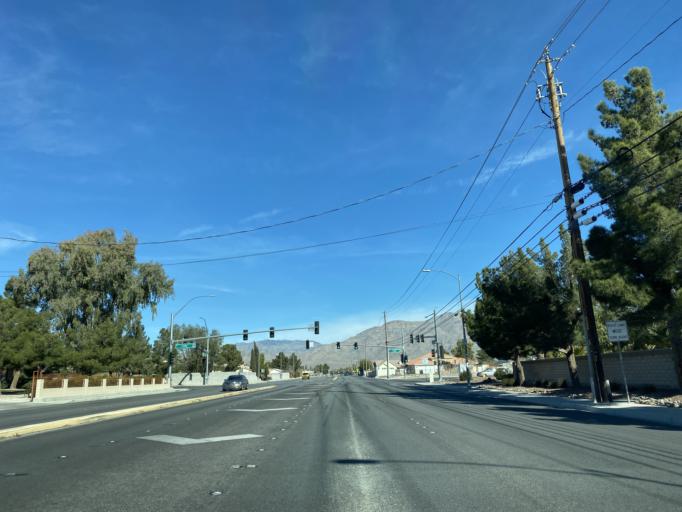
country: US
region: Nevada
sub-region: Clark County
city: North Las Vegas
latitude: 36.2970
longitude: -115.2241
